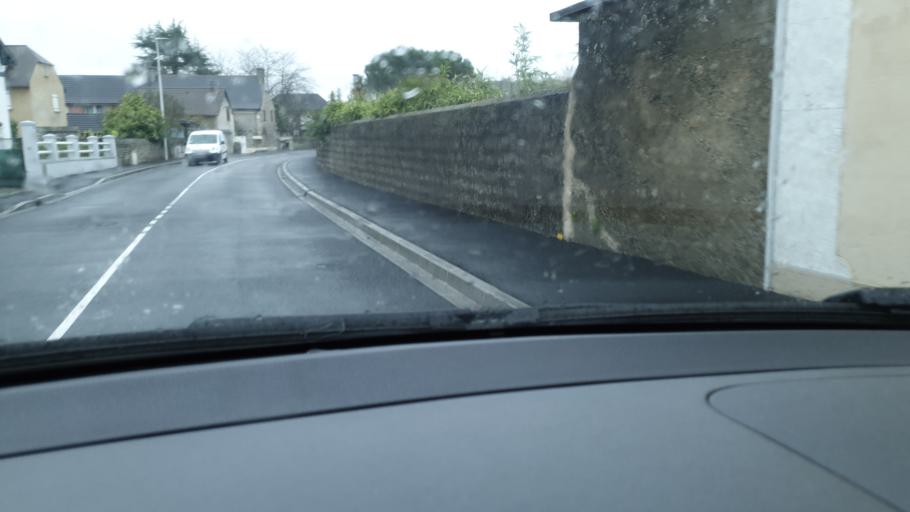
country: FR
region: Midi-Pyrenees
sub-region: Departement des Hautes-Pyrenees
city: Oursbelille
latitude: 43.2550
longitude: 0.0520
